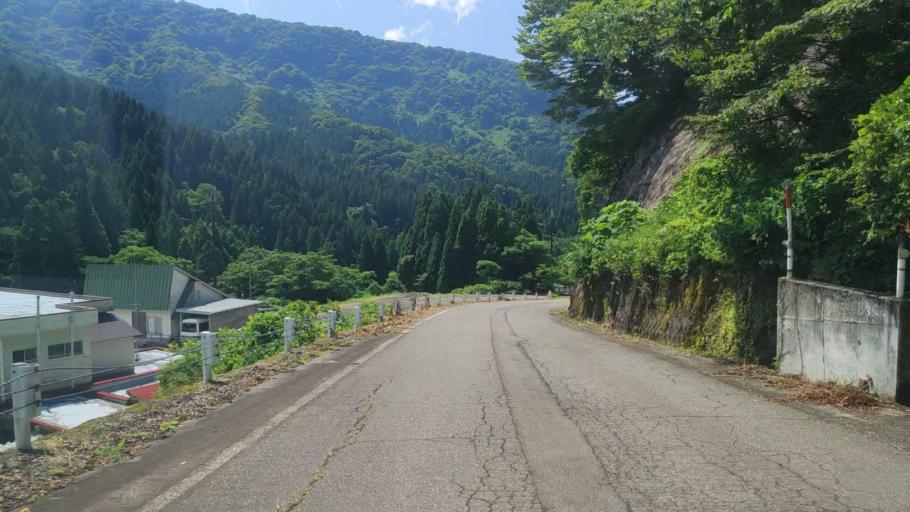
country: JP
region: Fukui
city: Katsuyama
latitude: 36.1222
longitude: 136.5075
